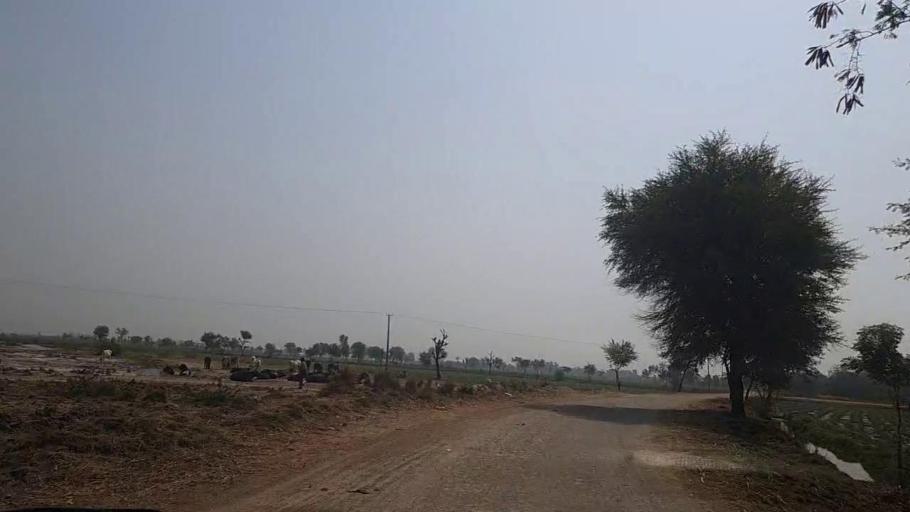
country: PK
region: Sindh
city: Pithoro
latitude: 25.5556
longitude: 69.2485
